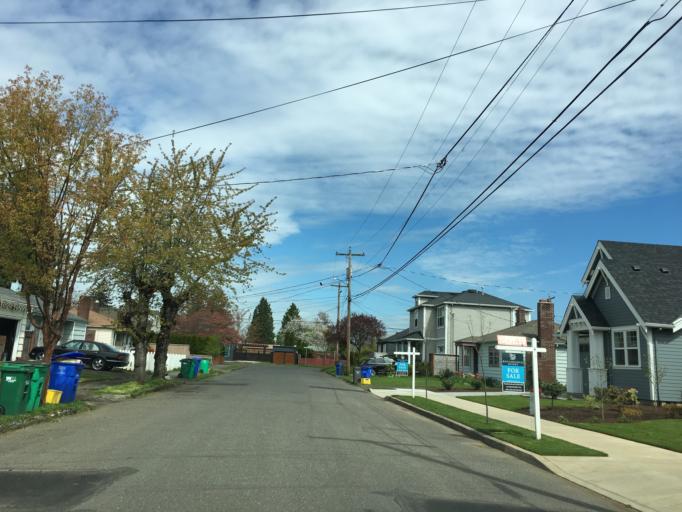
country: US
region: Oregon
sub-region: Multnomah County
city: Lents
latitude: 45.5296
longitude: -122.5914
